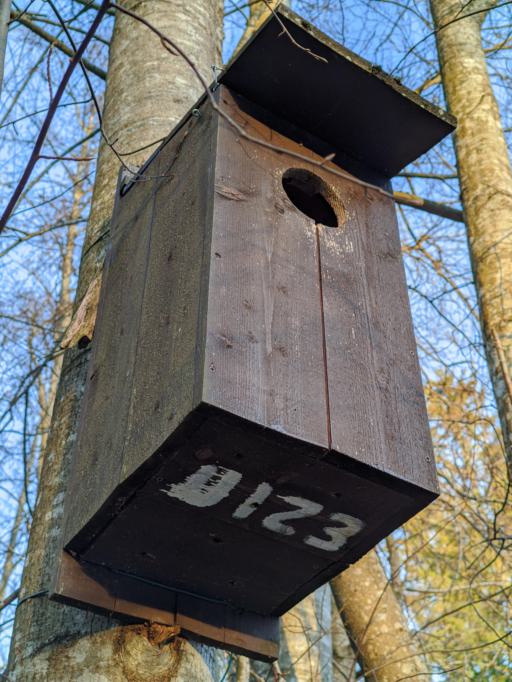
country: NO
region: Akershus
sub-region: Nannestad
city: Teigebyen
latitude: 60.1522
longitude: 11.0402
